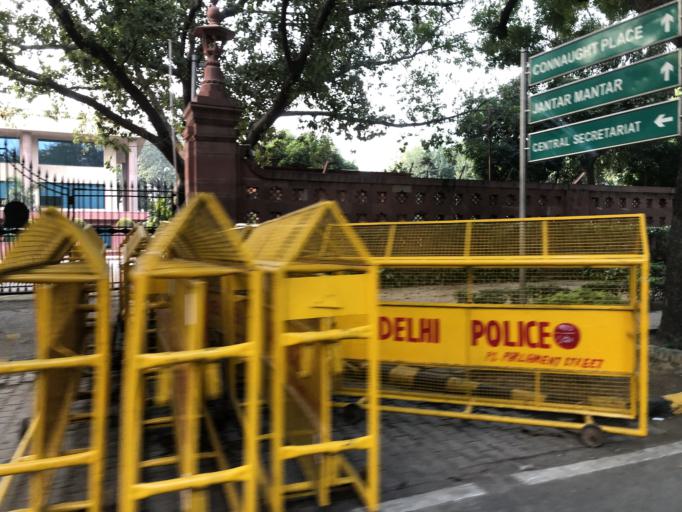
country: IN
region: NCT
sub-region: New Delhi
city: New Delhi
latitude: 28.6198
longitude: 77.2100
